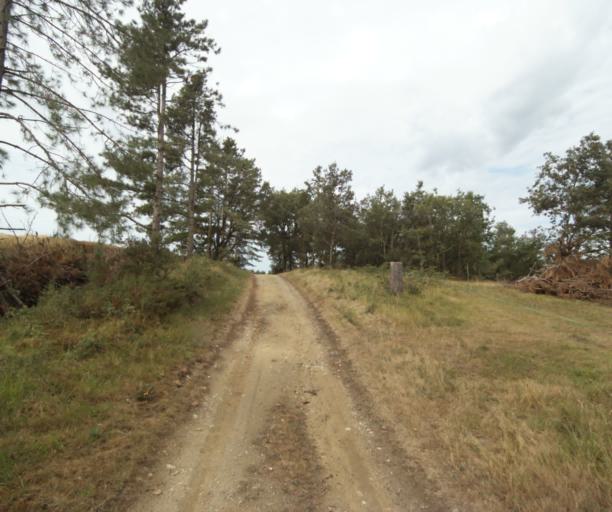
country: FR
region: Midi-Pyrenees
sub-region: Departement de la Haute-Garonne
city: Revel
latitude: 43.4402
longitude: 1.9831
